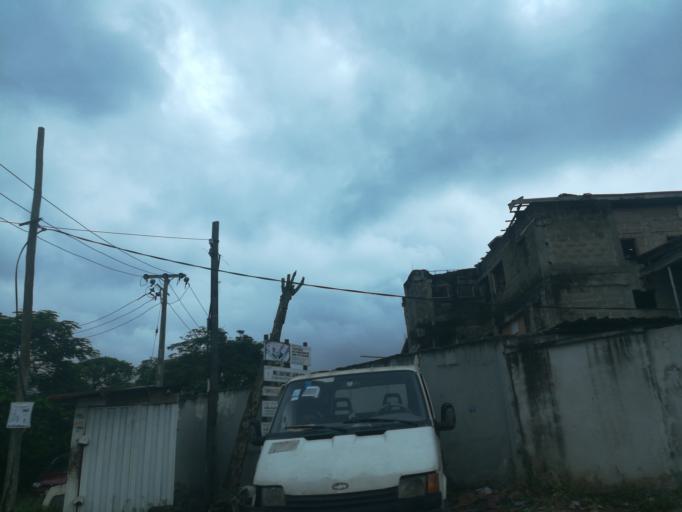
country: NG
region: Lagos
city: Ikeja
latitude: 6.6178
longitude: 3.3473
